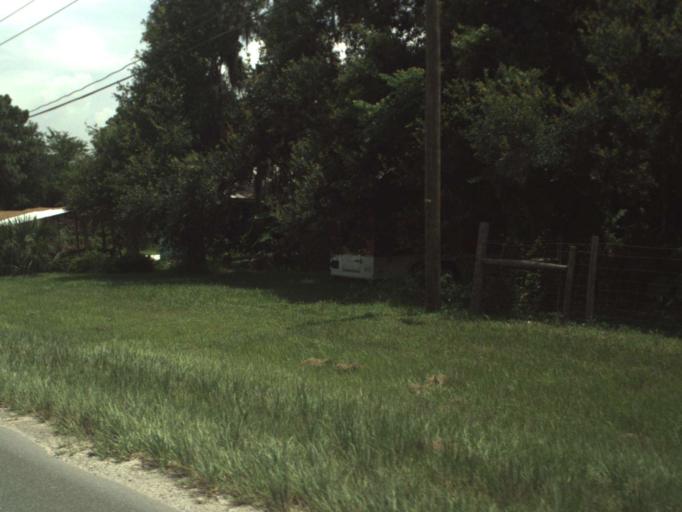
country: US
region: Florida
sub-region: Sumter County
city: Wildwood
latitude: 28.8120
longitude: -82.0455
